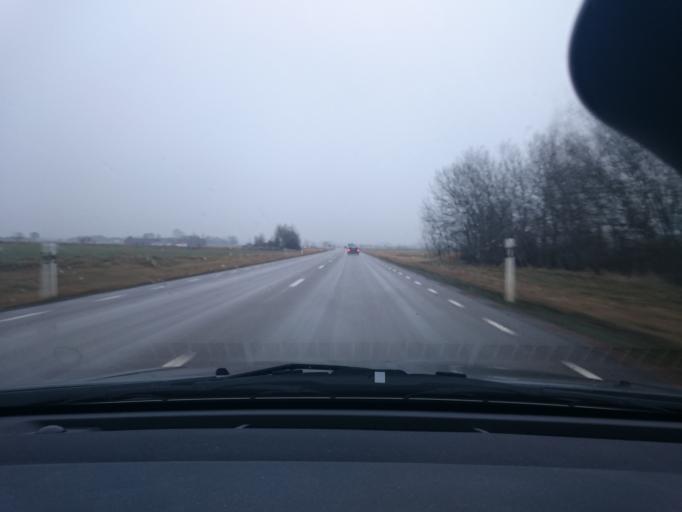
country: SE
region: Skane
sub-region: Bastads Kommun
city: Forslov
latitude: 56.3267
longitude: 12.8288
